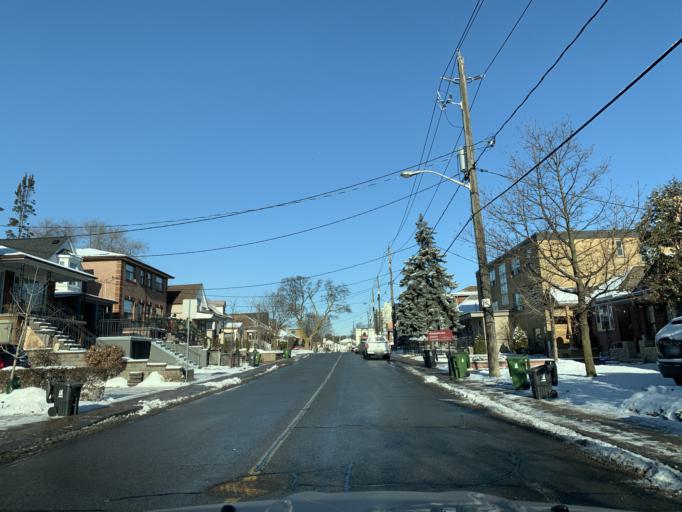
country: CA
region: Ontario
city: Toronto
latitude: 43.6808
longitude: -79.4910
